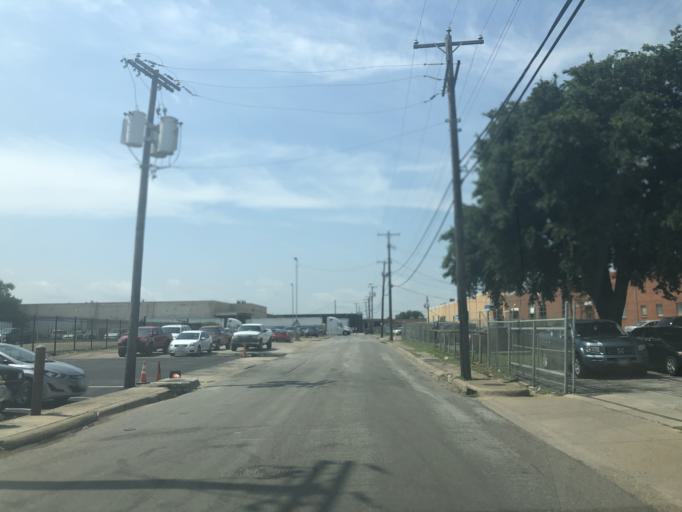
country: US
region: Texas
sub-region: Dallas County
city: Dallas
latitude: 32.8060
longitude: -96.8672
